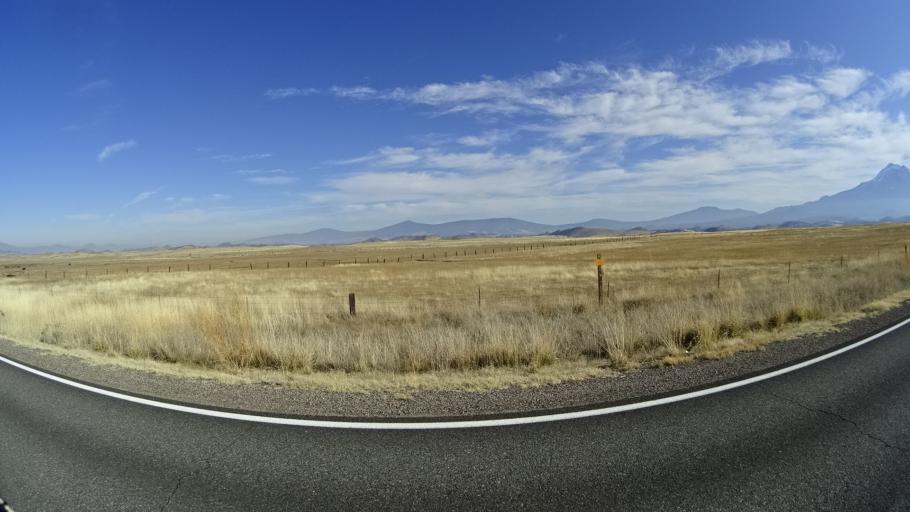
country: US
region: California
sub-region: Siskiyou County
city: Weed
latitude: 41.4861
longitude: -122.5009
